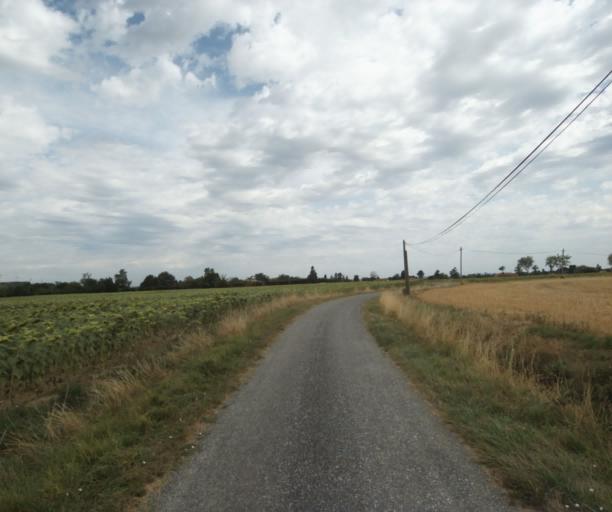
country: FR
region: Midi-Pyrenees
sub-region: Departement de la Haute-Garonne
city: Saint-Felix-Lauragais
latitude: 43.4449
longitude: 1.9362
